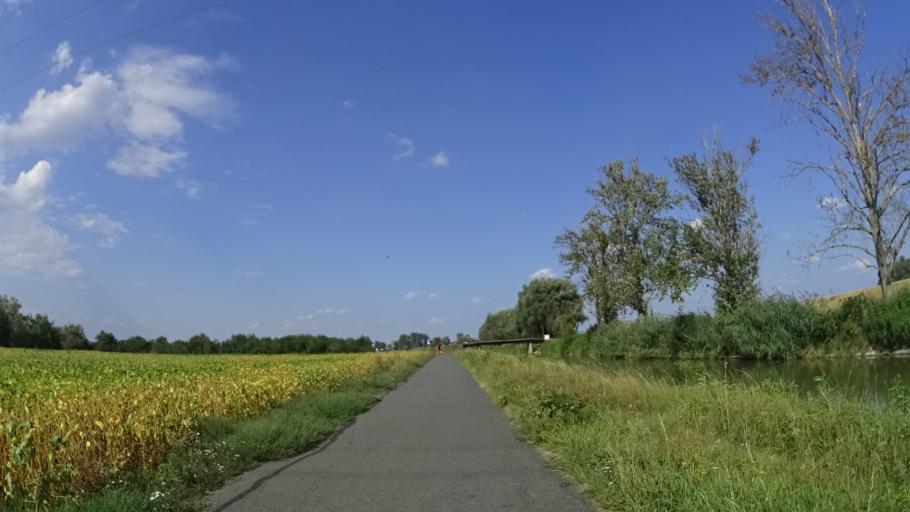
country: CZ
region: Zlin
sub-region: Okres Uherske Hradiste
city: Uherske Hradiste
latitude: 49.0776
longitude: 17.4585
